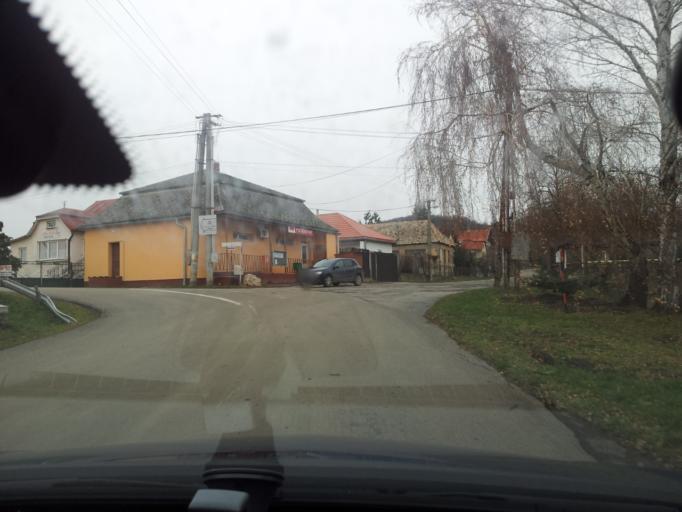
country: HU
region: Borsod-Abauj-Zemplen
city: Satoraljaujhely
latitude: 48.4551
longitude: 21.6818
